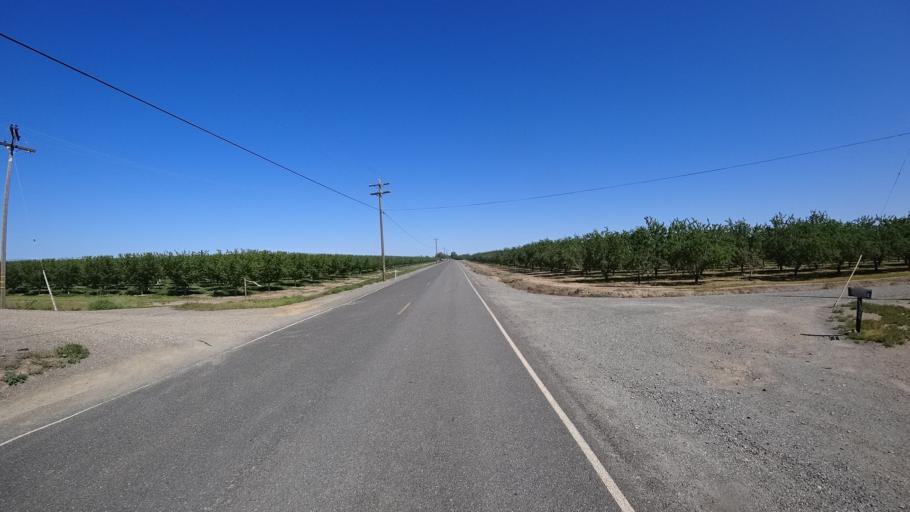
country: US
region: California
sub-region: Glenn County
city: Hamilton City
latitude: 39.6993
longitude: -122.1034
